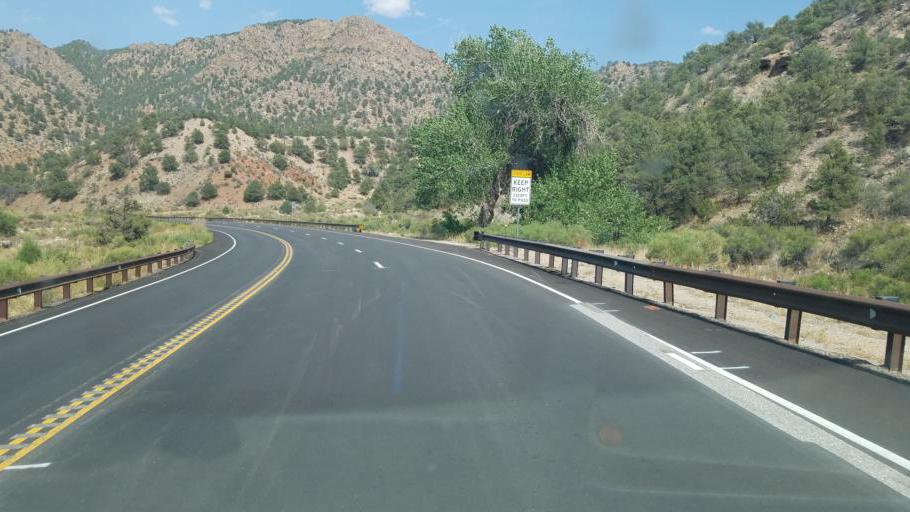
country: US
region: Colorado
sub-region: Custer County
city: Westcliffe
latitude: 38.4093
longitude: -105.5799
